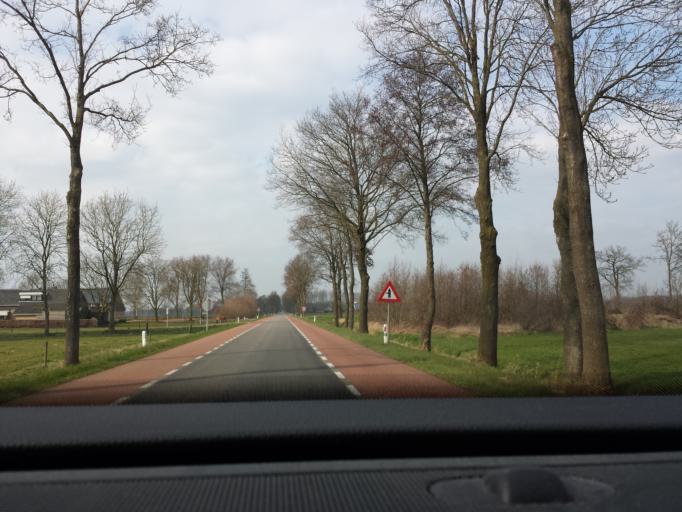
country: NL
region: Gelderland
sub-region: Berkelland
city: Borculo
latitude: 52.0358
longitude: 6.4851
